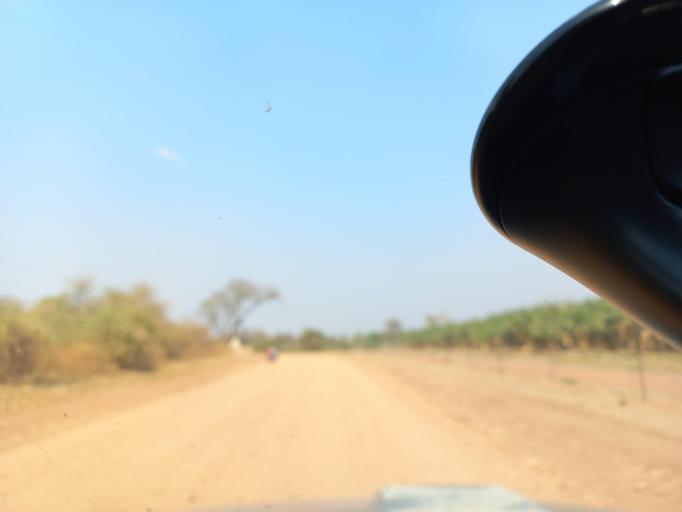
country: ZW
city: Chirundu
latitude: -15.9306
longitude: 28.9626
